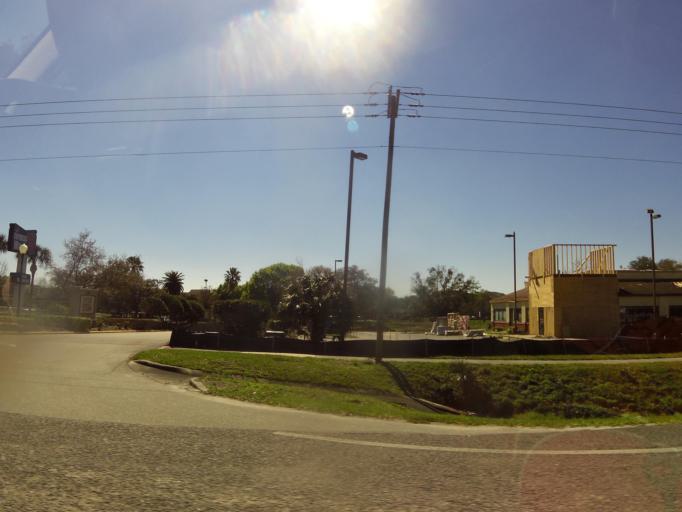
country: US
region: Florida
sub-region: Orange County
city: Lockhart
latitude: 28.6071
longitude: -81.4237
